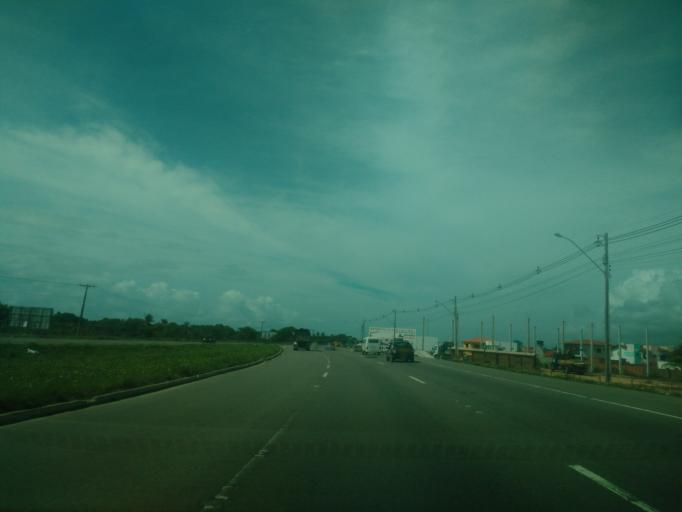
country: BR
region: Alagoas
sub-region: Marechal Deodoro
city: Marechal Deodoro
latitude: -9.7413
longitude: -35.8364
